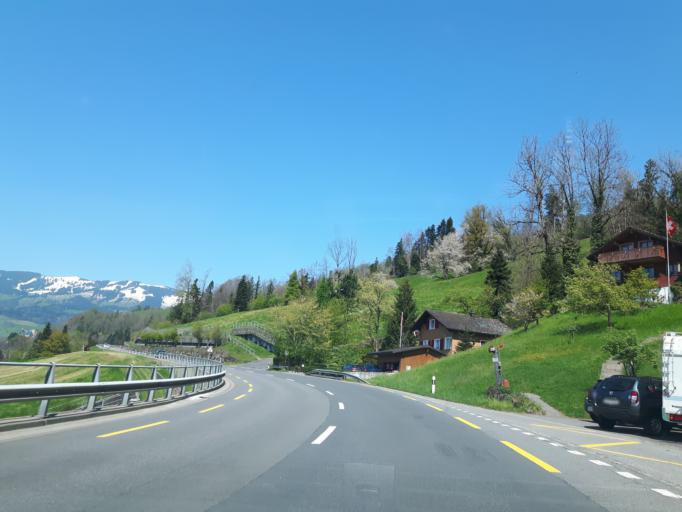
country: CH
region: Schwyz
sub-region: Bezirk Schwyz
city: Schwyz
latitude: 47.0393
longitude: 8.6405
